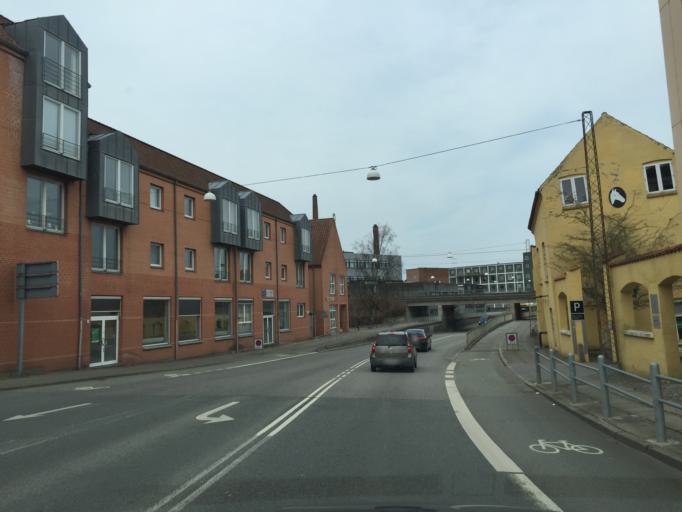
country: DK
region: South Denmark
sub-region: Kolding Kommune
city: Kolding
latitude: 55.4868
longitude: 9.4719
